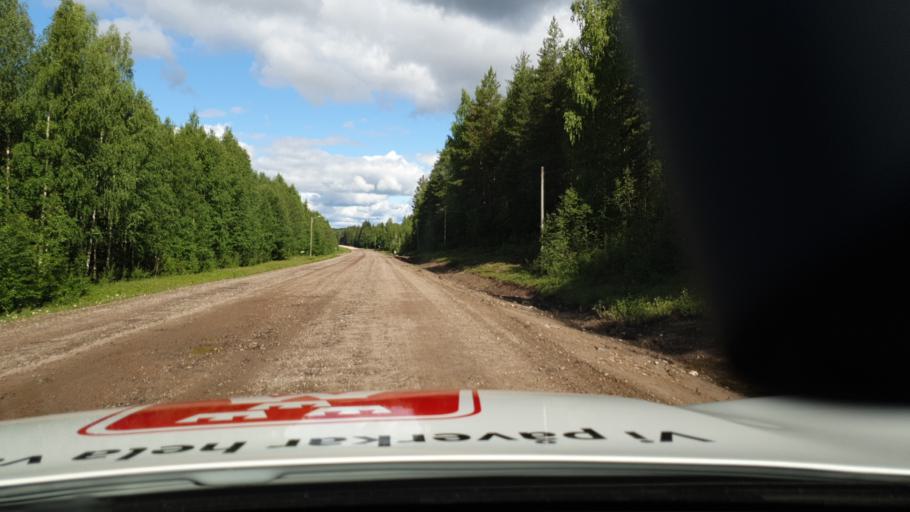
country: SE
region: Norrbotten
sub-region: Alvsbyns Kommun
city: AElvsbyn
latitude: 66.1280
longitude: 20.9117
